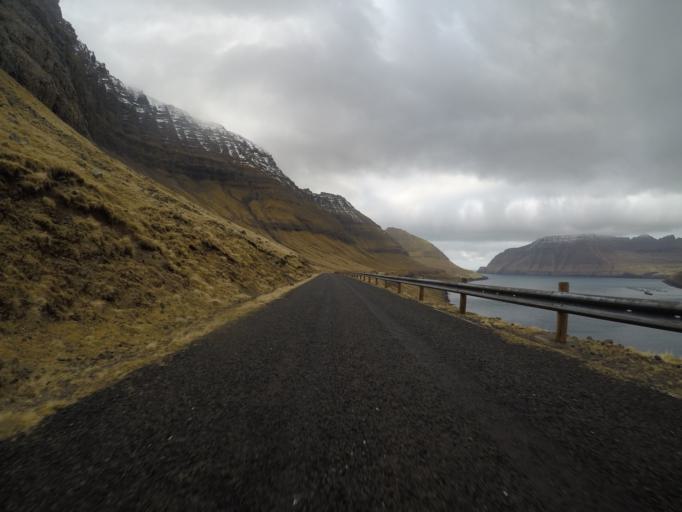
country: FO
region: Nordoyar
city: Klaksvik
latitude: 62.3295
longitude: -6.5709
